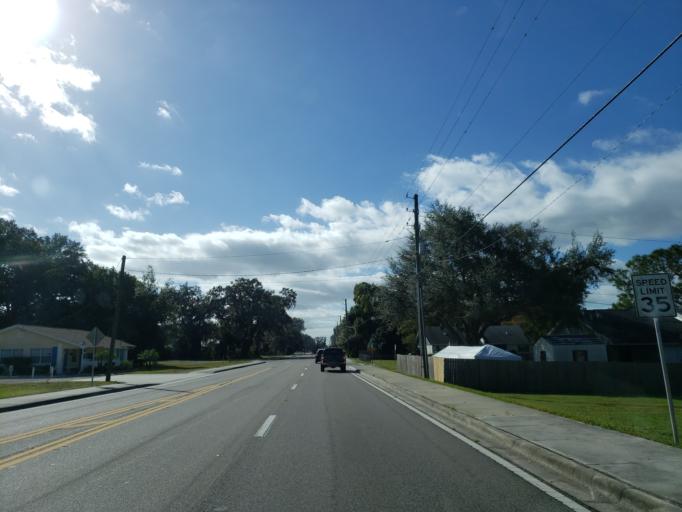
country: US
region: Florida
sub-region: Polk County
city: Medulla
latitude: 27.9815
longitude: -81.9733
